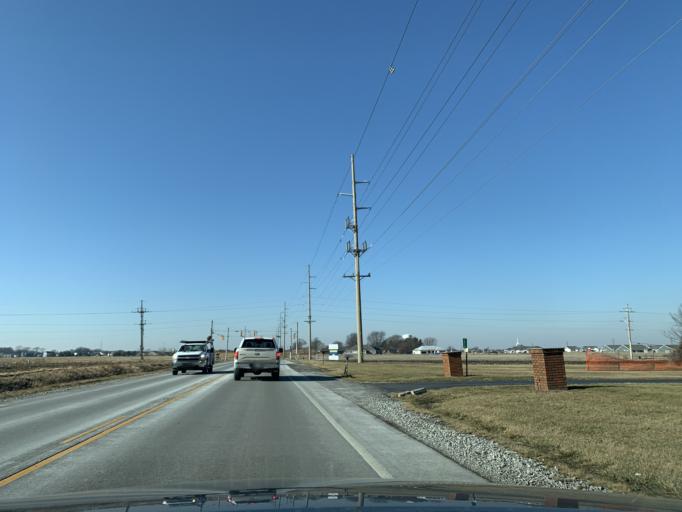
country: US
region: Indiana
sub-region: Lake County
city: Saint John
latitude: 41.4209
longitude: -87.4294
